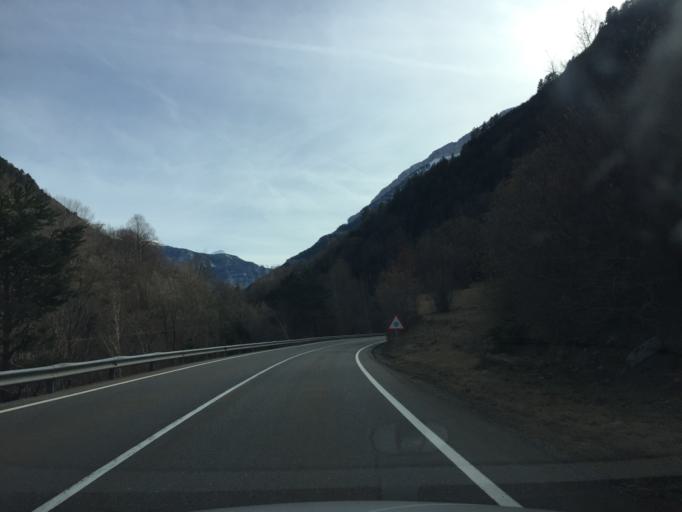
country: ES
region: Aragon
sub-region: Provincia de Huesca
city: Bielsa
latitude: 42.6455
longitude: 0.2118
